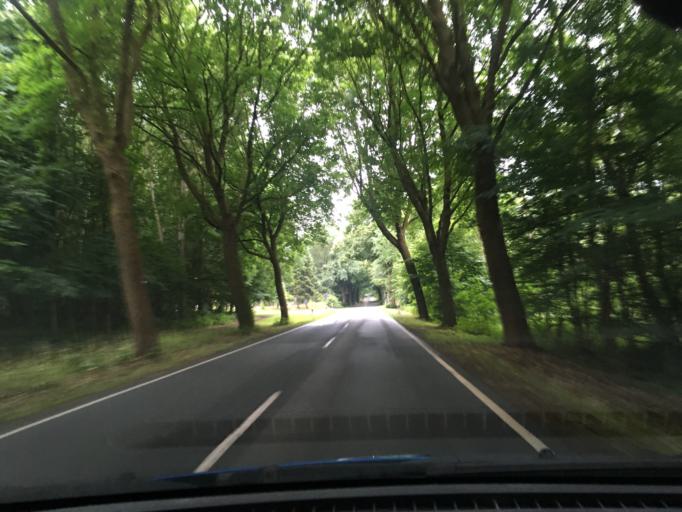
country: DE
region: Lower Saxony
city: Garlstorf
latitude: 53.2274
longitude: 10.0892
